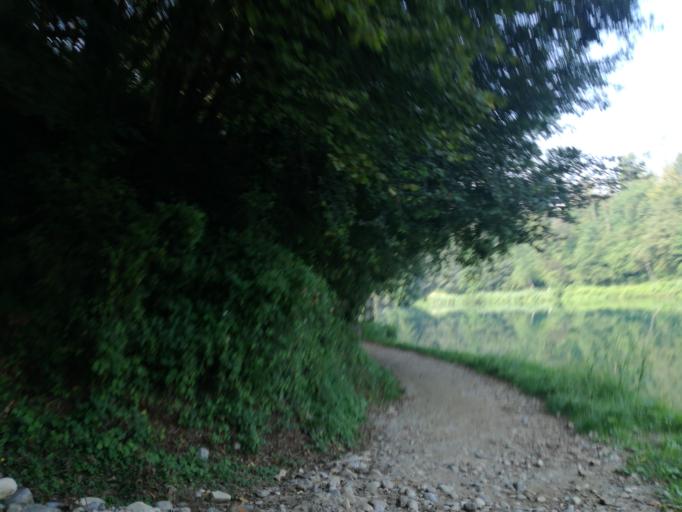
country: IT
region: Lombardy
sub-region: Provincia di Bergamo
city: Villa d'Adda
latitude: 45.7103
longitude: 9.4529
